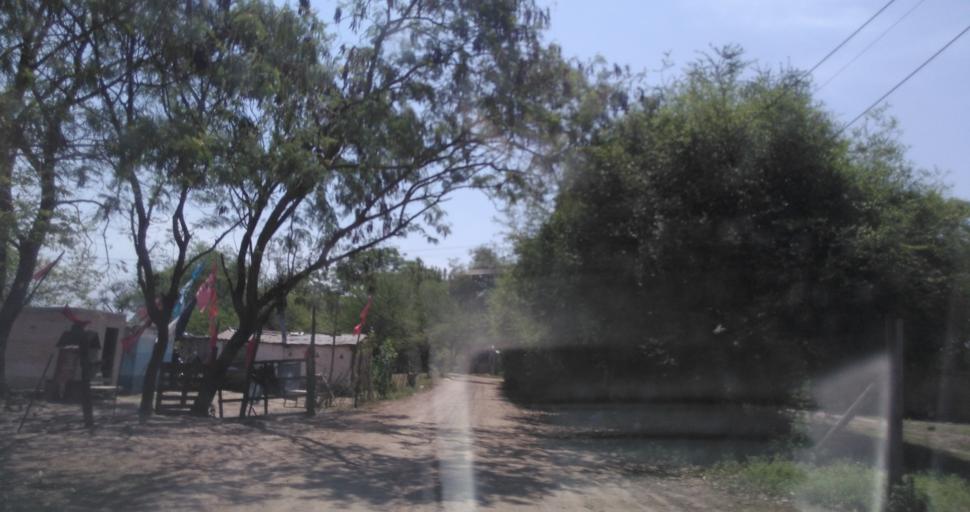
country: AR
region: Chaco
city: Fontana
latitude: -27.4170
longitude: -59.0108
